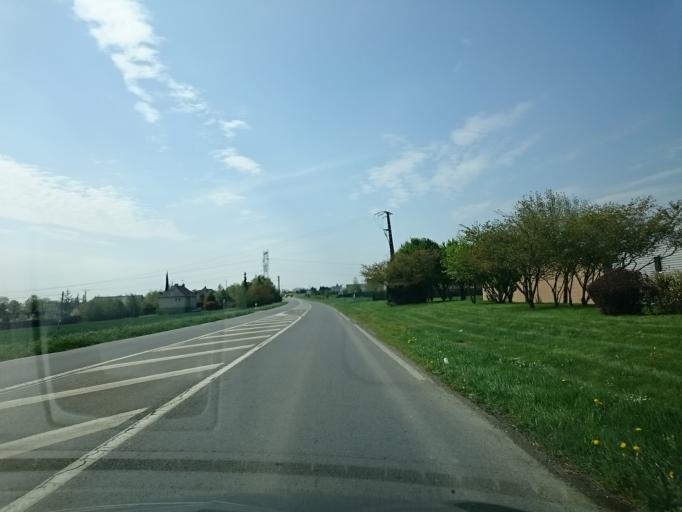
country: FR
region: Brittany
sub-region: Departement d'Ille-et-Vilaine
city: Nouvoitou
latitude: 48.0562
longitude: -1.5297
